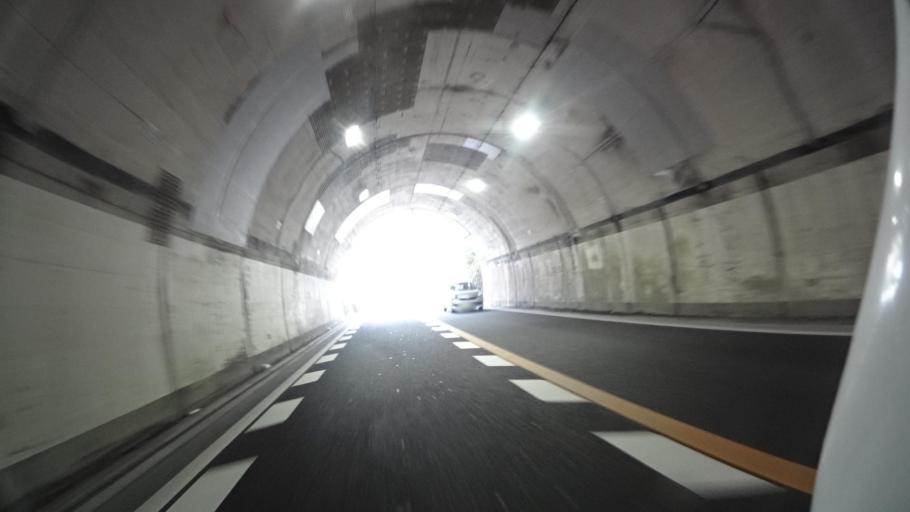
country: JP
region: Wakayama
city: Shingu
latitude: 33.4818
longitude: 135.7502
